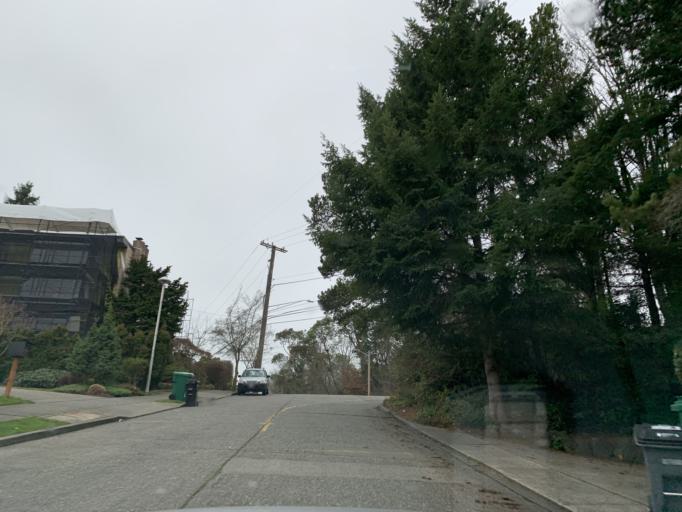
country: US
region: Washington
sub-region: King County
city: Yarrow Point
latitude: 47.6685
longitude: -122.2724
